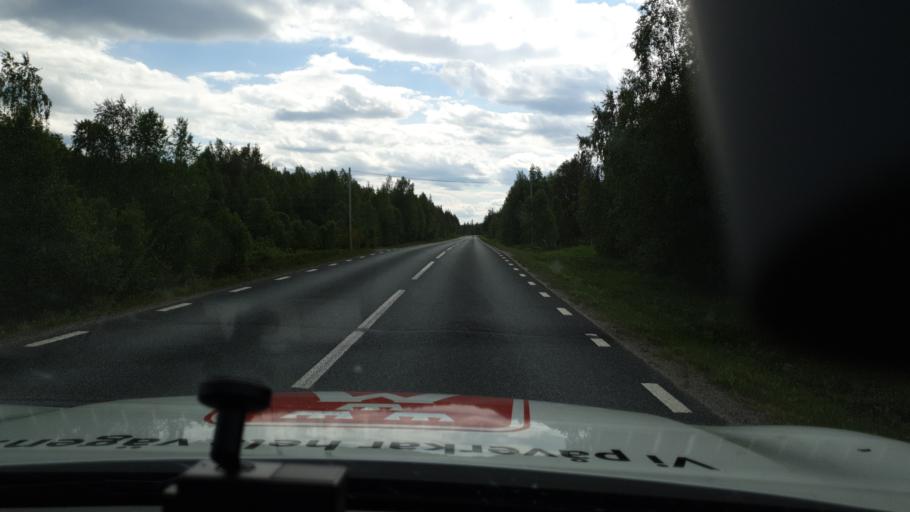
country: SE
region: Vaesterbotten
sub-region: Sorsele Kommun
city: Sorsele
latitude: 65.3717
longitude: 17.5760
